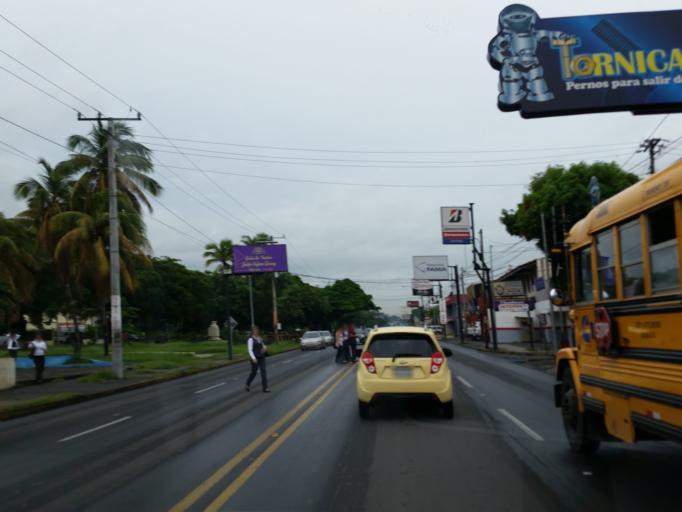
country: NI
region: Managua
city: Managua
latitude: 12.1459
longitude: -86.2896
